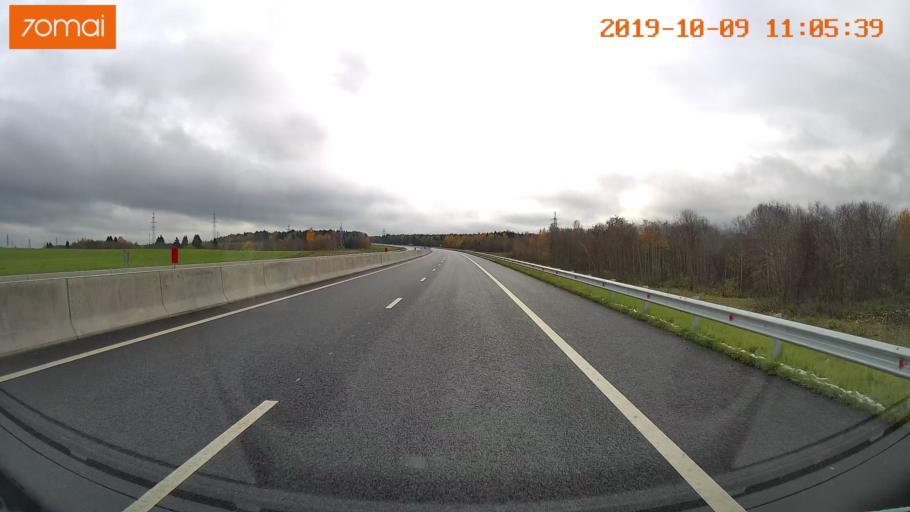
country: RU
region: Vologda
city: Molochnoye
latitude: 59.1970
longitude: 39.7580
